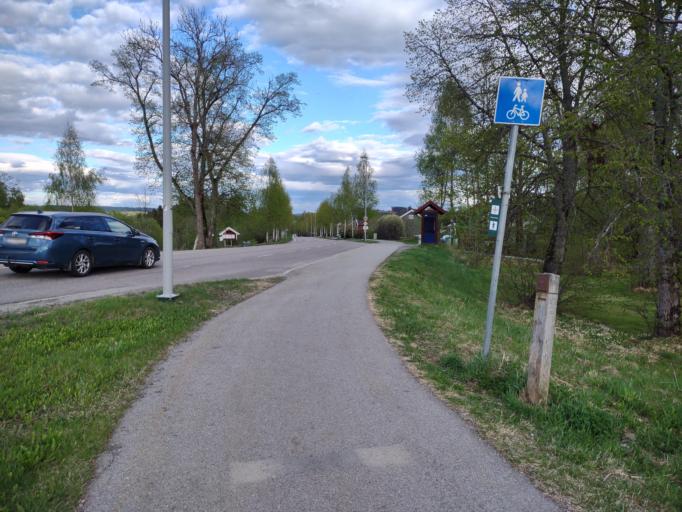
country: NO
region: Akershus
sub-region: Eidsvoll
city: Eidsvoll
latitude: 60.3239
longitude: 11.2297
